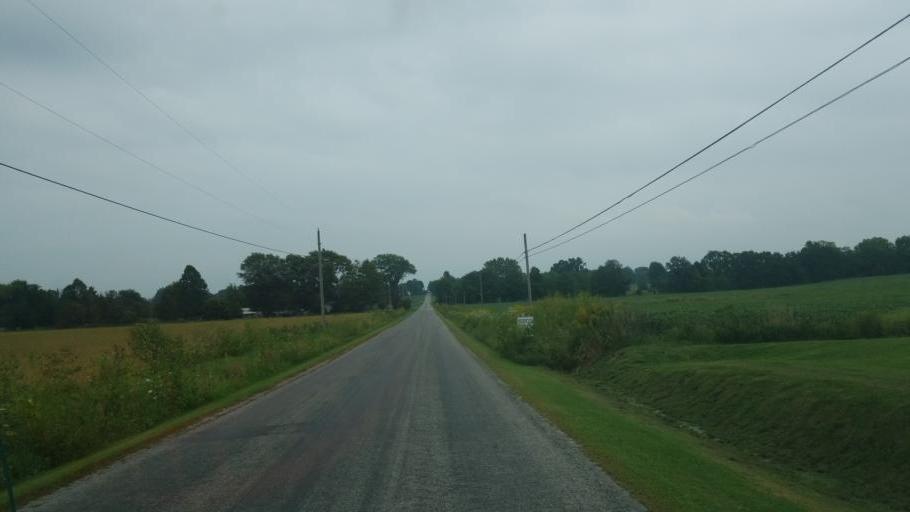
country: US
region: Ohio
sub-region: Wayne County
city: Creston
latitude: 40.9599
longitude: -81.9130
